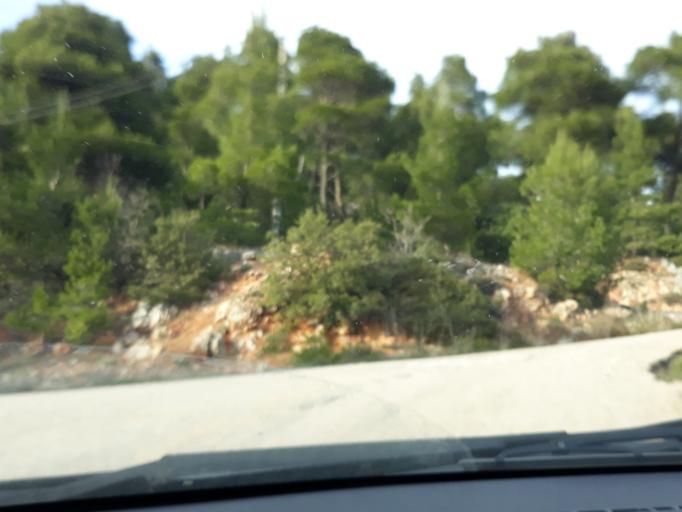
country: GR
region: Attica
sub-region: Nomarchia Anatolikis Attikis
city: Afidnes
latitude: 38.2127
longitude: 23.8157
